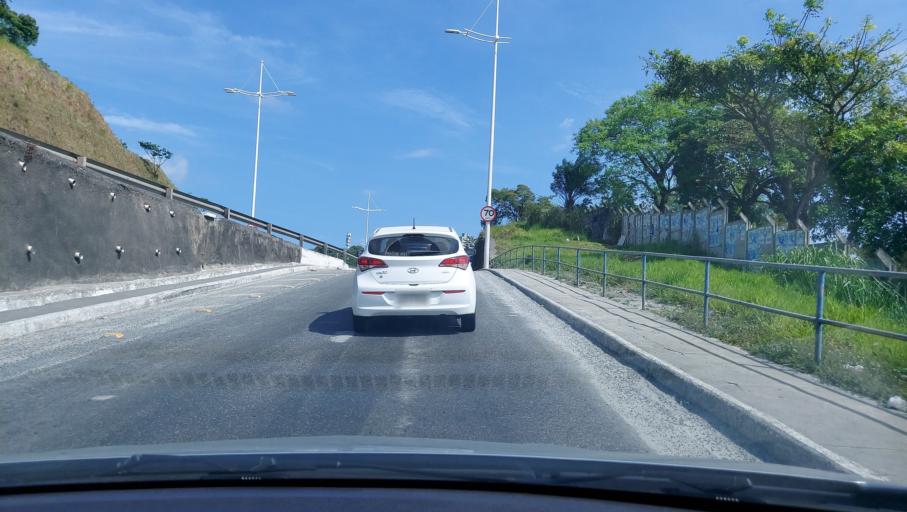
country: BR
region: Bahia
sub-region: Salvador
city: Salvador
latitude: -12.9529
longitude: -38.4741
